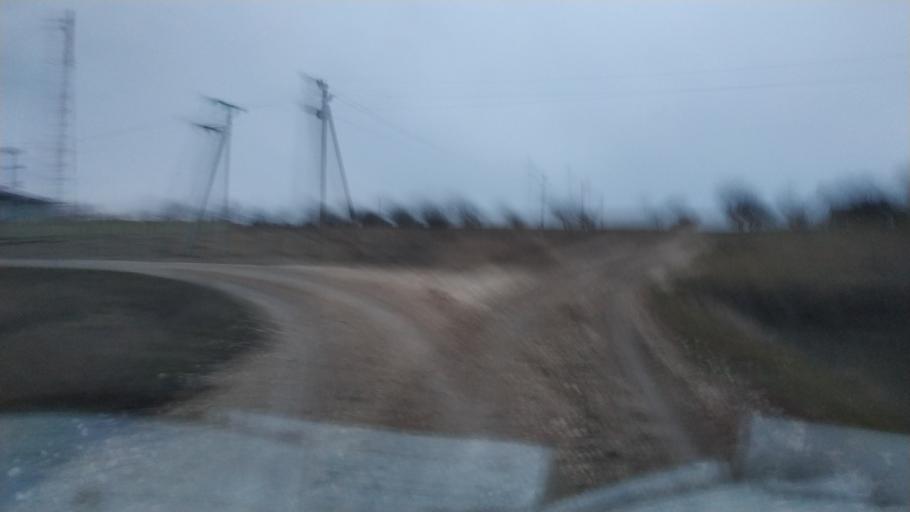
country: MD
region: Causeni
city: Causeni
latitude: 46.4927
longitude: 29.3975
